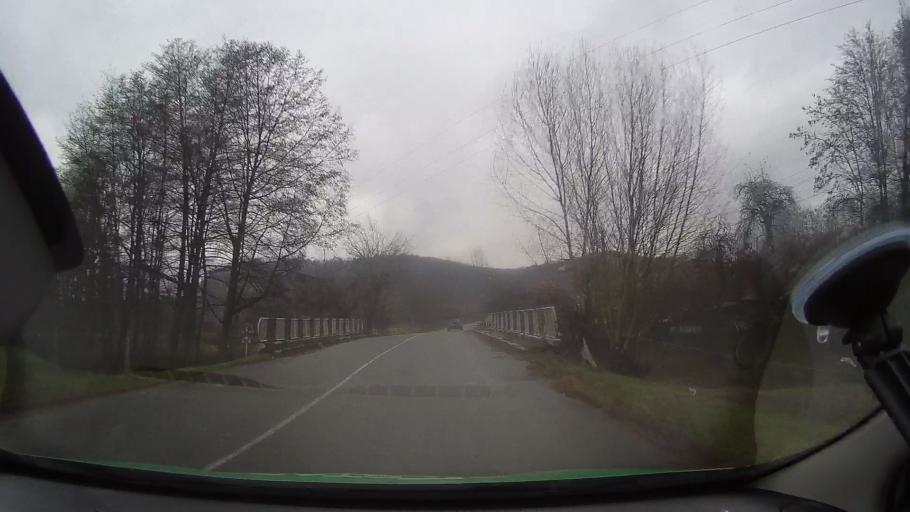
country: RO
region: Hunedoara
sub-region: Comuna Tomesti
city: Tomesti
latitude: 46.1983
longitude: 22.6521
